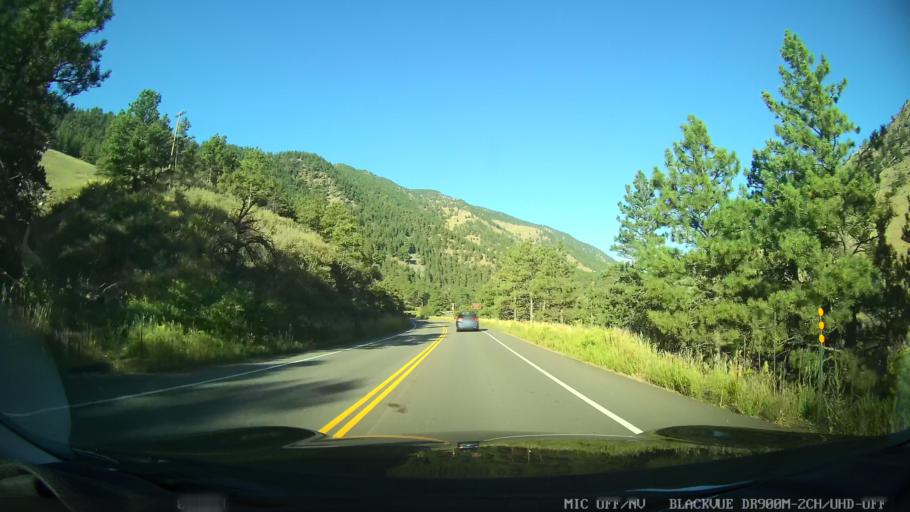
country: US
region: Colorado
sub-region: Boulder County
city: Lyons
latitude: 40.4199
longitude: -105.2767
